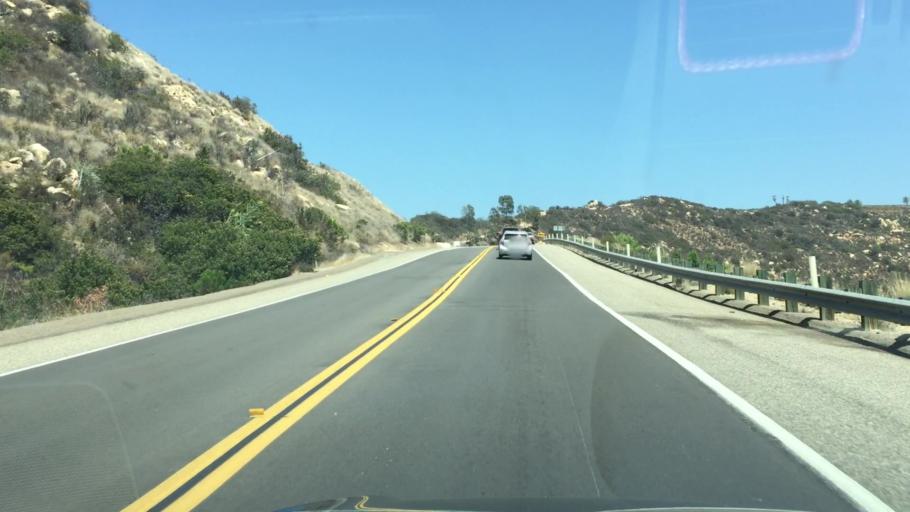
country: US
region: California
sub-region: San Diego County
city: Jamul
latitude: 32.7344
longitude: -116.8345
